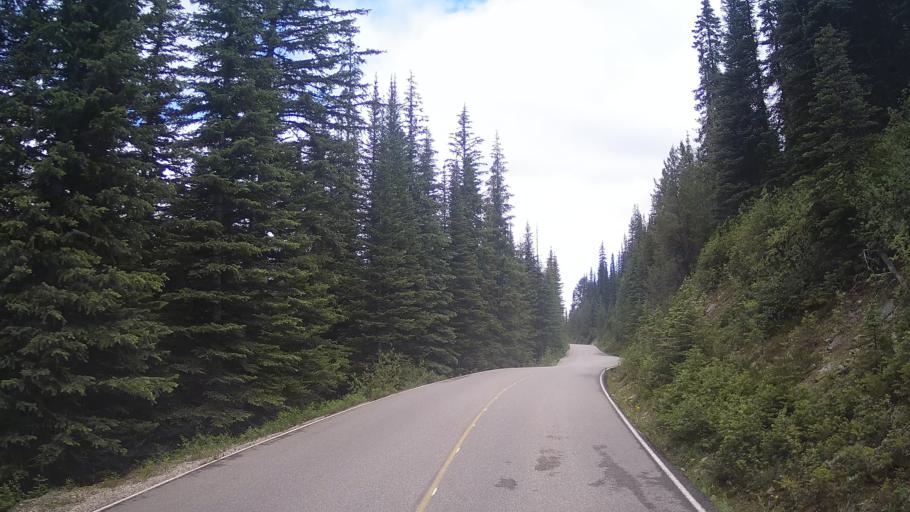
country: CA
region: Alberta
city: Jasper Park Lodge
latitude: 52.6921
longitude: -118.0576
